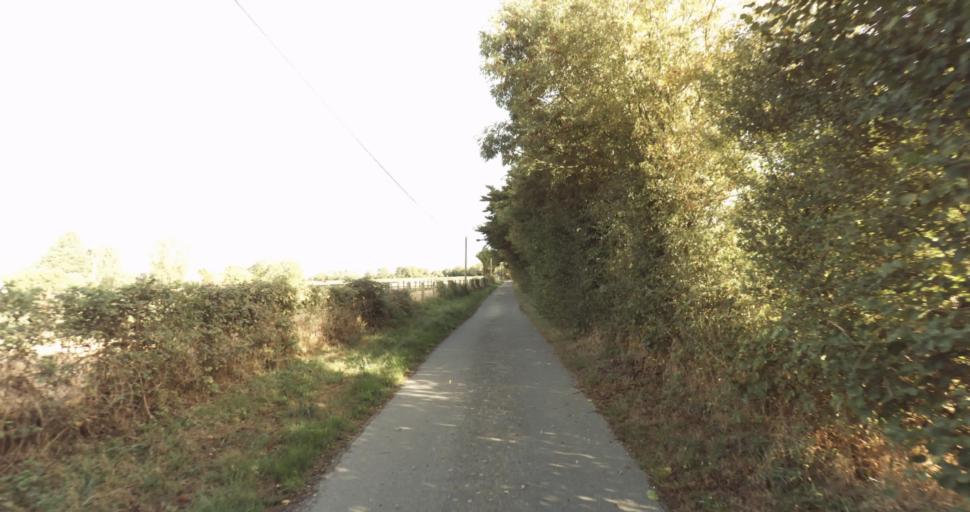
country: FR
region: Lower Normandy
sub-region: Departement de l'Orne
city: Vimoutiers
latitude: 48.8763
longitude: 0.2501
